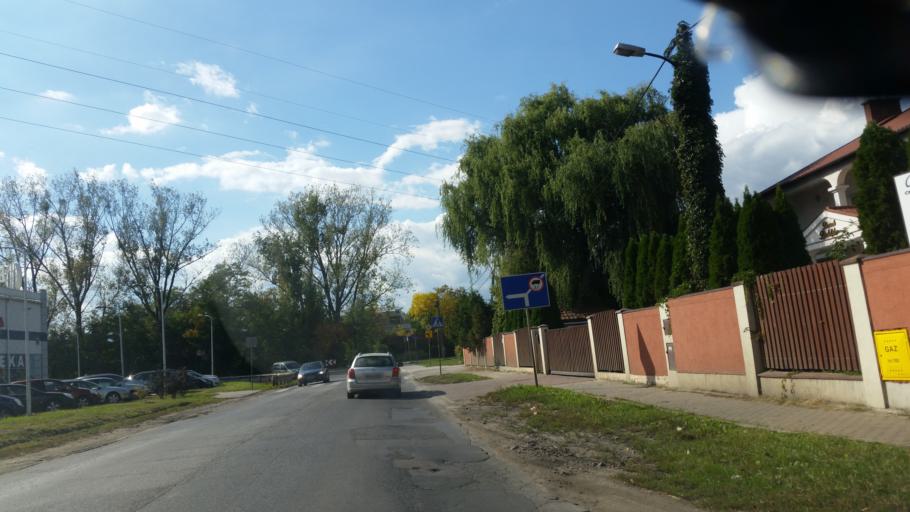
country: PL
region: Masovian Voivodeship
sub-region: Warszawa
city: Targowek
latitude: 52.3177
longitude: 21.0306
